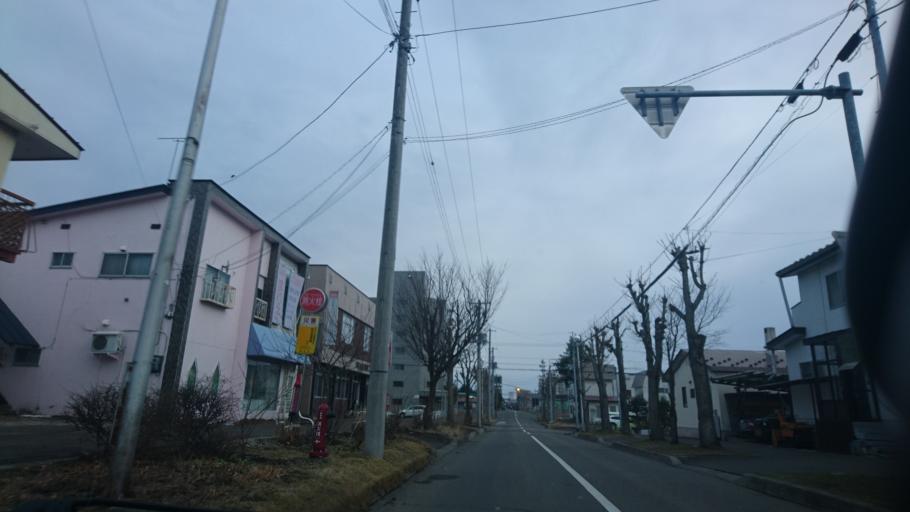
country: JP
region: Hokkaido
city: Obihiro
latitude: 42.9304
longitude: 143.1978
